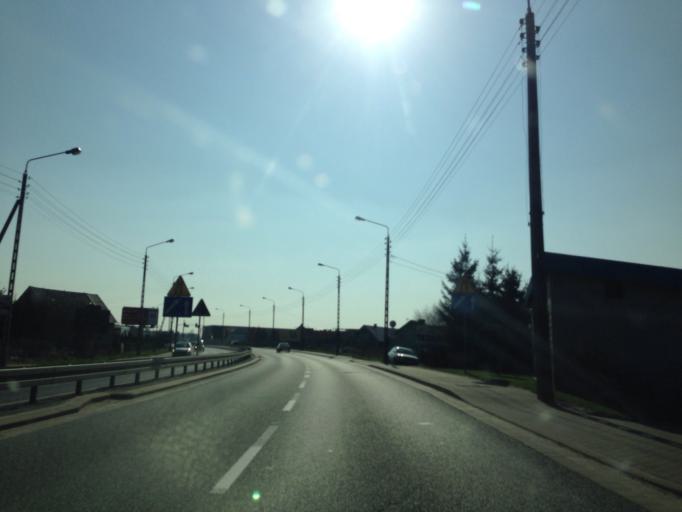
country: PL
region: Lower Silesian Voivodeship
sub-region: Powiat wroclawski
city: Dlugoleka
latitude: 51.1894
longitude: 17.2297
